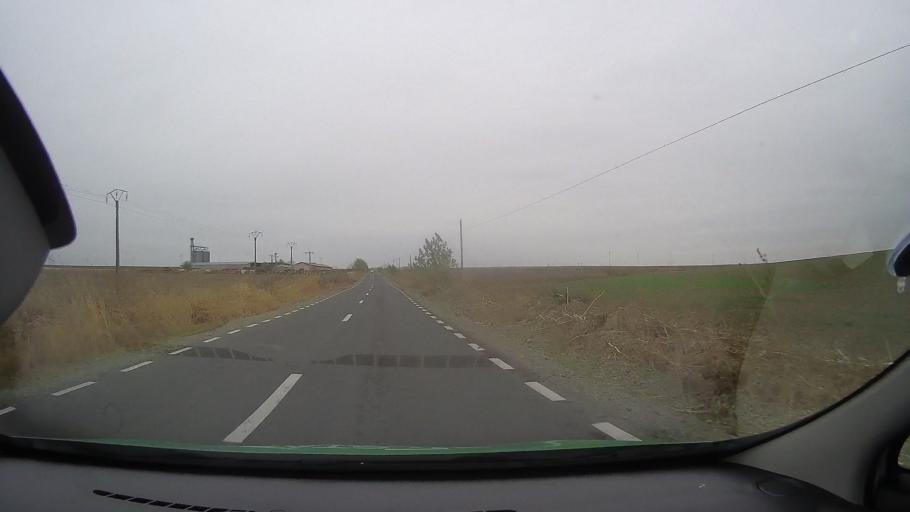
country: RO
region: Constanta
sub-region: Comuna Tortoman
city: Tortoman
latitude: 44.3613
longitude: 28.2100
